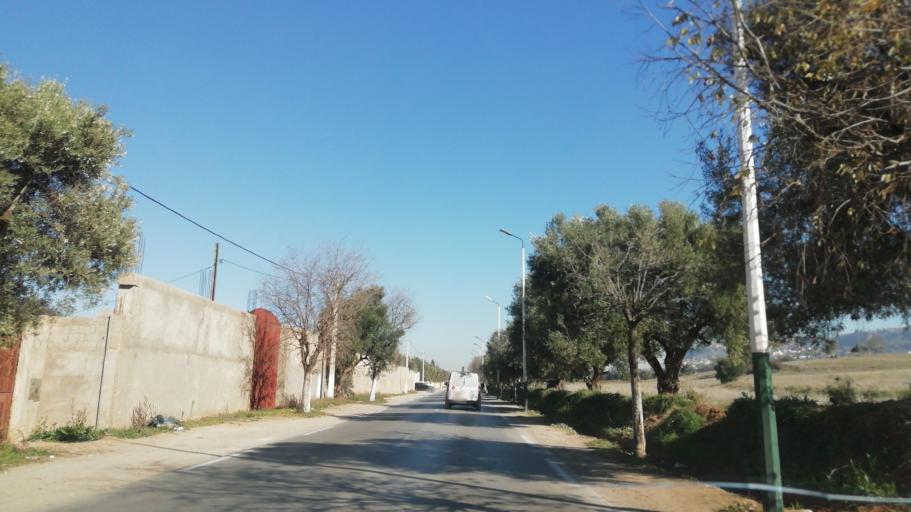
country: DZ
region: Tlemcen
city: Mansoura
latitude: 34.8640
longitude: -1.3564
